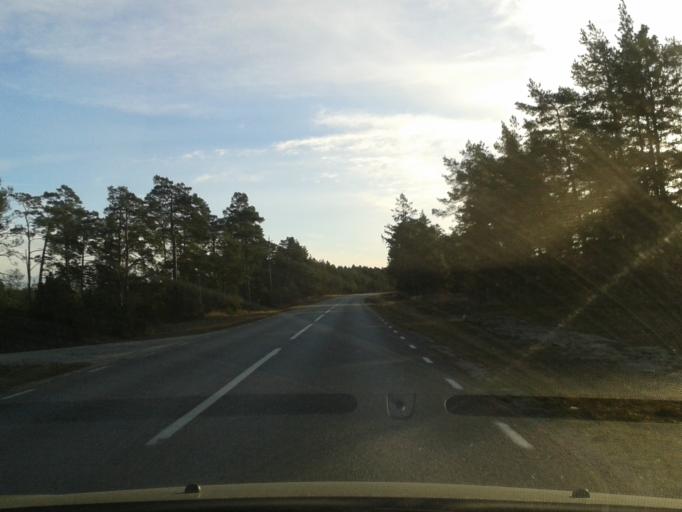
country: SE
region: Gotland
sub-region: Gotland
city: Hemse
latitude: 57.3481
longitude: 18.6906
